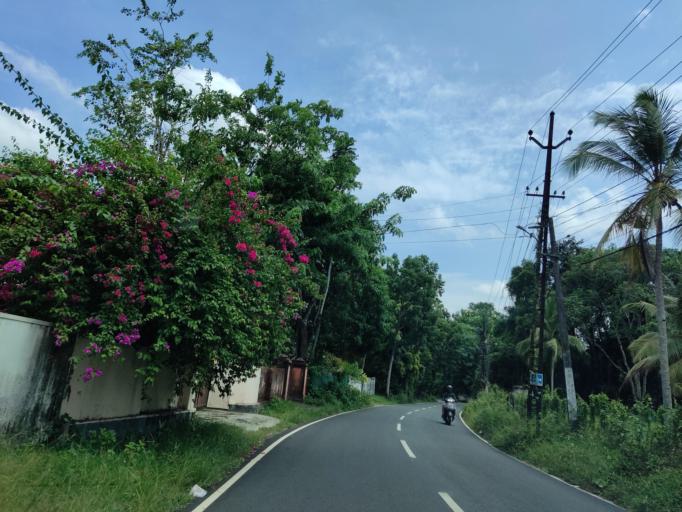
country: IN
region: Kerala
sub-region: Alappuzha
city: Mavelikara
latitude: 9.2673
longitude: 76.5623
